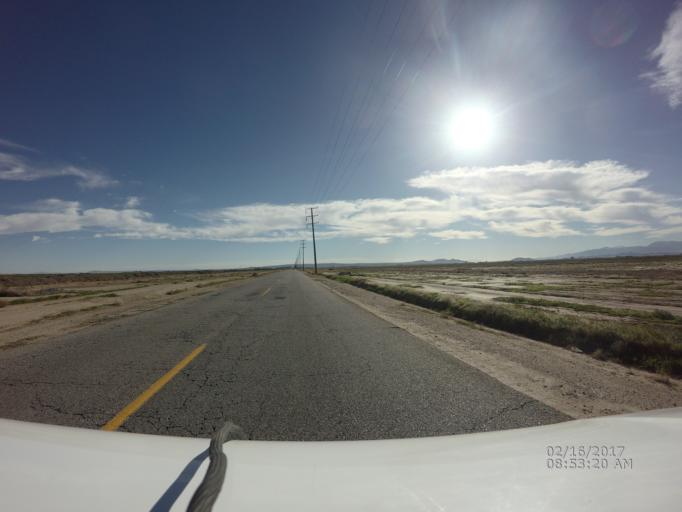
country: US
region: California
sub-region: Kern County
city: Edwards Air Force Base
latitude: 34.7637
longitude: -117.9855
